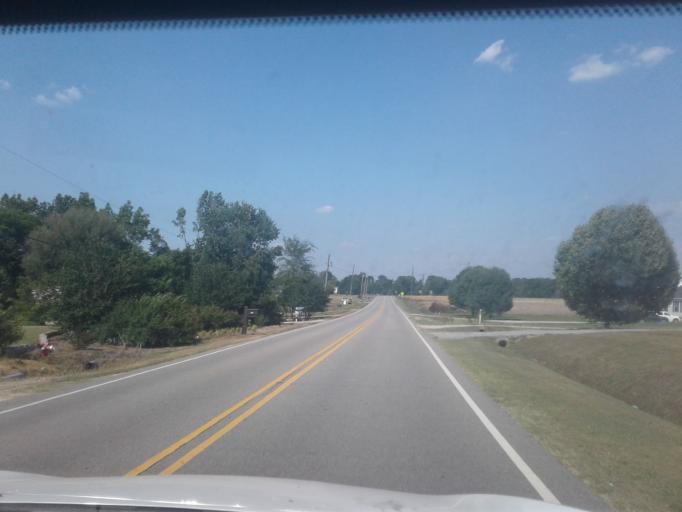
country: US
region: North Carolina
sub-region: Harnett County
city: Erwin
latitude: 35.3371
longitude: -78.6502
